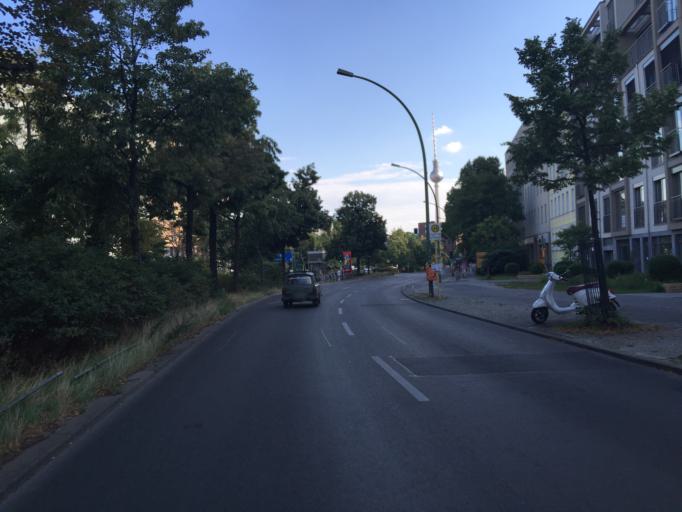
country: DE
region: Berlin
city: Berlin
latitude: 52.5337
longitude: 13.4127
